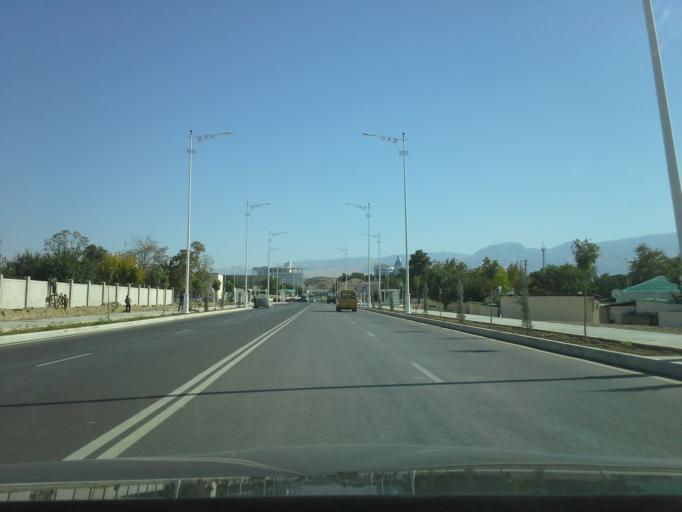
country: TM
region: Ahal
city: Ashgabat
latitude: 37.9606
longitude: 58.3398
